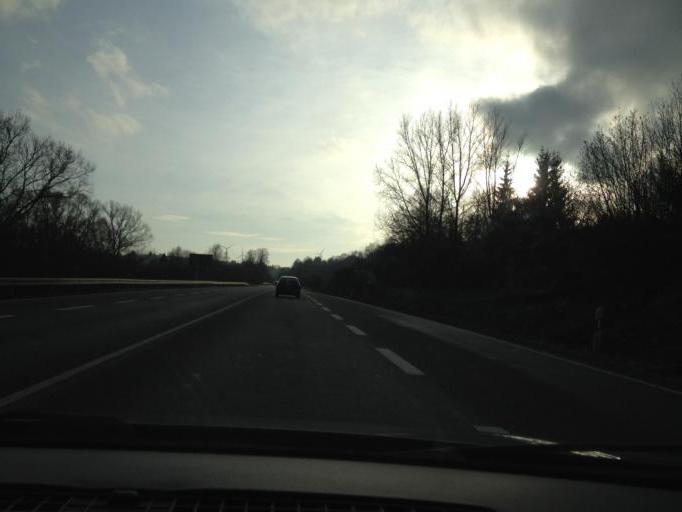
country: DE
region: Saarland
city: Ottweiler
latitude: 49.4230
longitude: 7.1617
